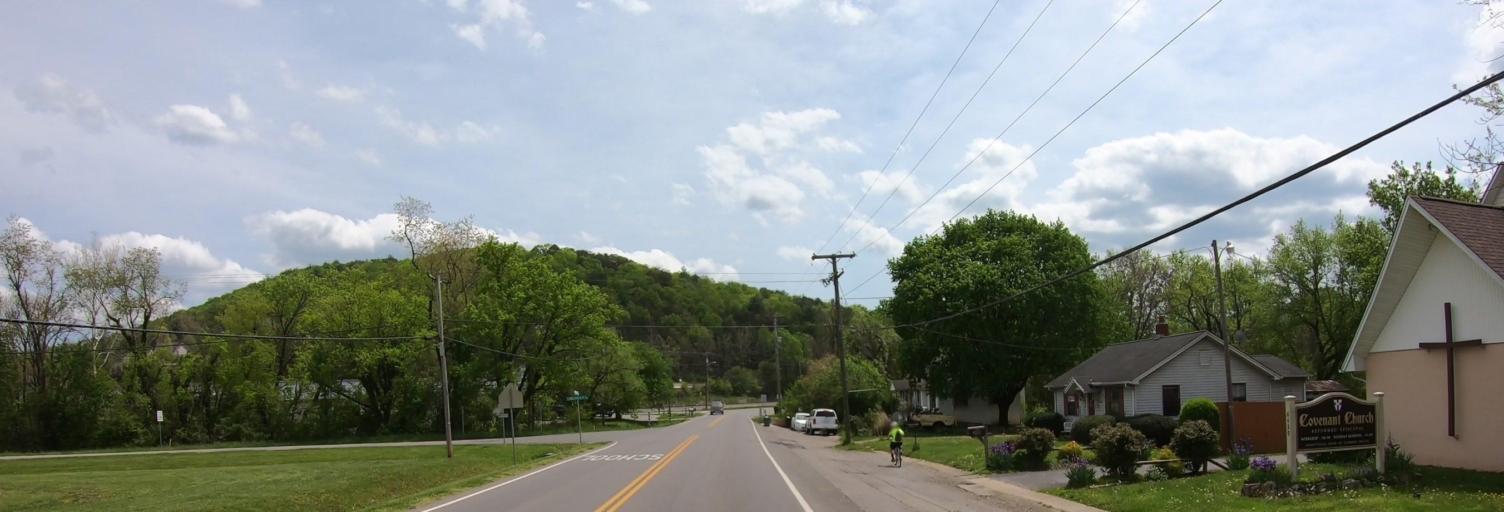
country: US
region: Virginia
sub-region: Roanoke County
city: Cave Spring
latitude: 37.2024
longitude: -79.9992
